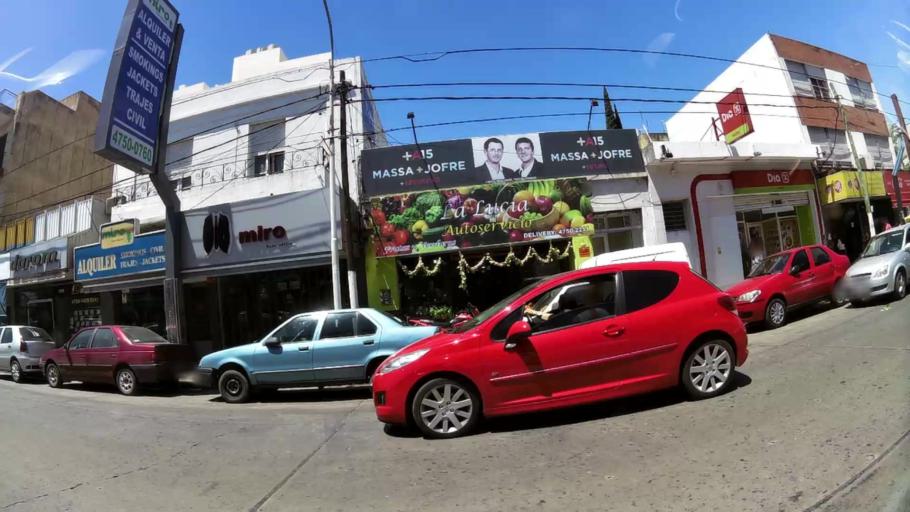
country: AR
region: Buenos Aires
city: Caseros
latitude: -34.6017
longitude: -58.5618
